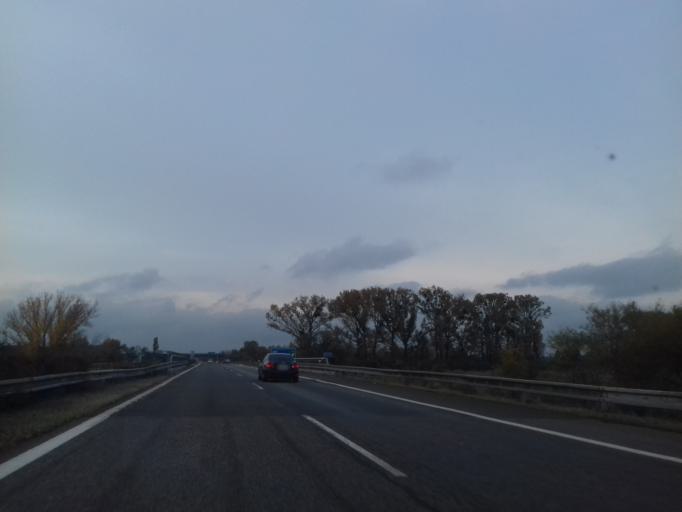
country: CZ
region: South Moravian
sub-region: Okres Breclav
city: Lanzhot
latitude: 48.6342
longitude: 17.0047
